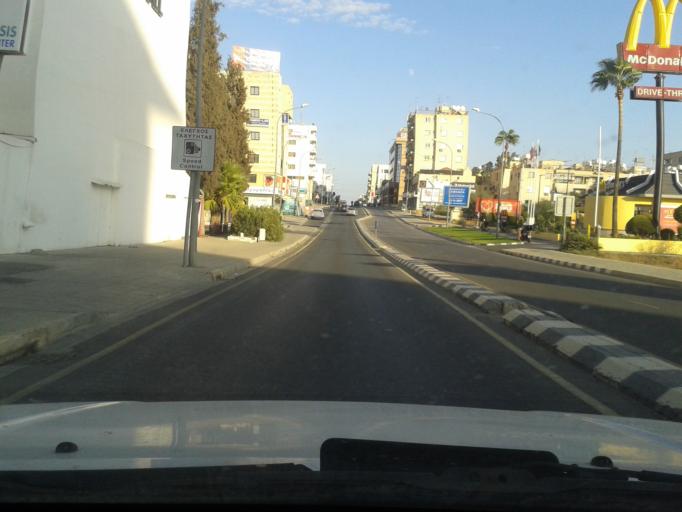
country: CY
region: Lefkosia
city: Nicosia
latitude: 35.1452
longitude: 33.3609
